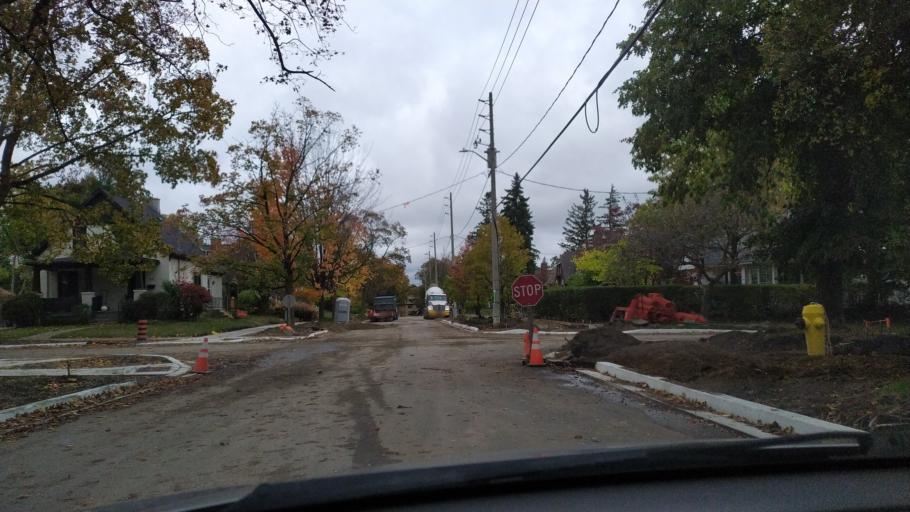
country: CA
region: Ontario
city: Waterloo
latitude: 43.4526
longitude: -80.5194
